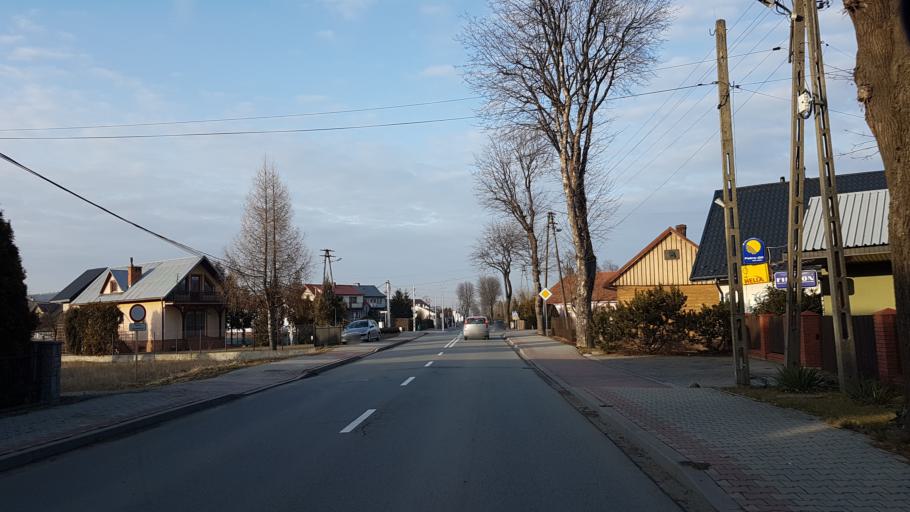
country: PL
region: Lesser Poland Voivodeship
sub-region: Powiat nowosadecki
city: Stary Sacz
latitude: 49.5414
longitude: 20.6449
